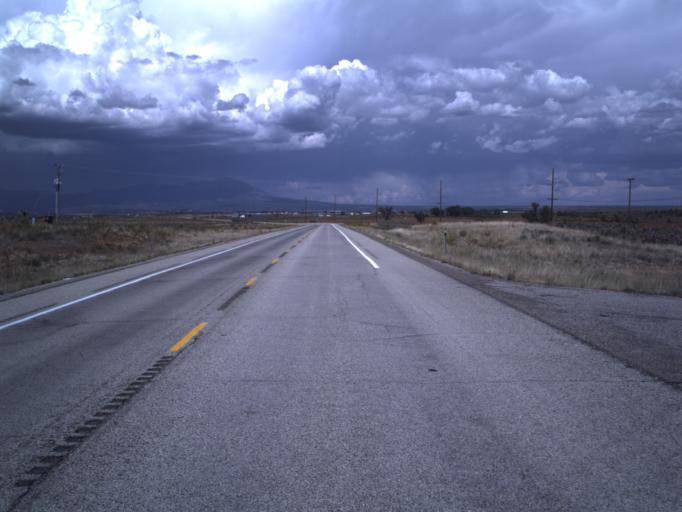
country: US
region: Utah
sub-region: San Juan County
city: Blanding
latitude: 37.5504
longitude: -109.4906
